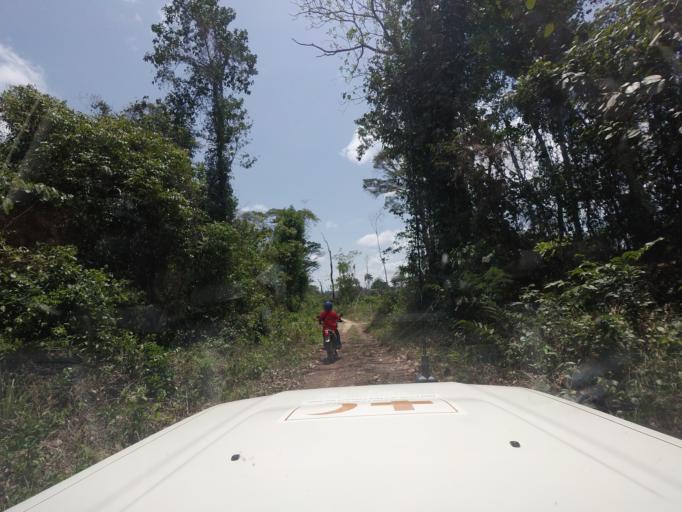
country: GN
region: Nzerekore
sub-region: Yomou
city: Yomou
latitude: 7.3758
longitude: -9.3085
